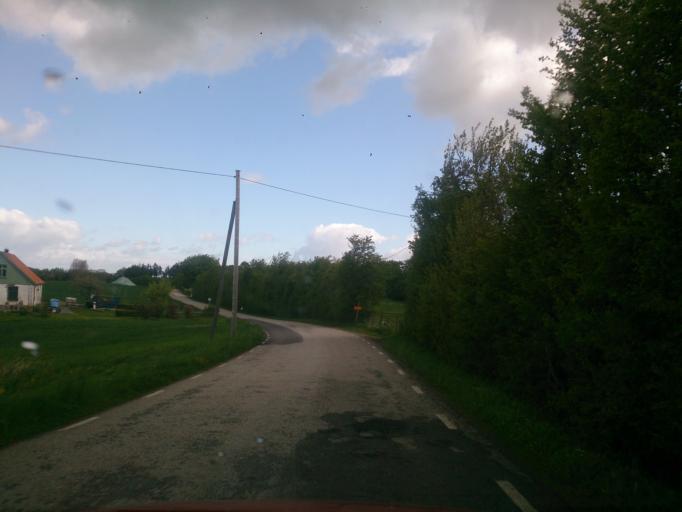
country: SE
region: Skane
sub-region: Ystads Kommun
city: Ystad
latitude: 55.4997
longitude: 13.7106
